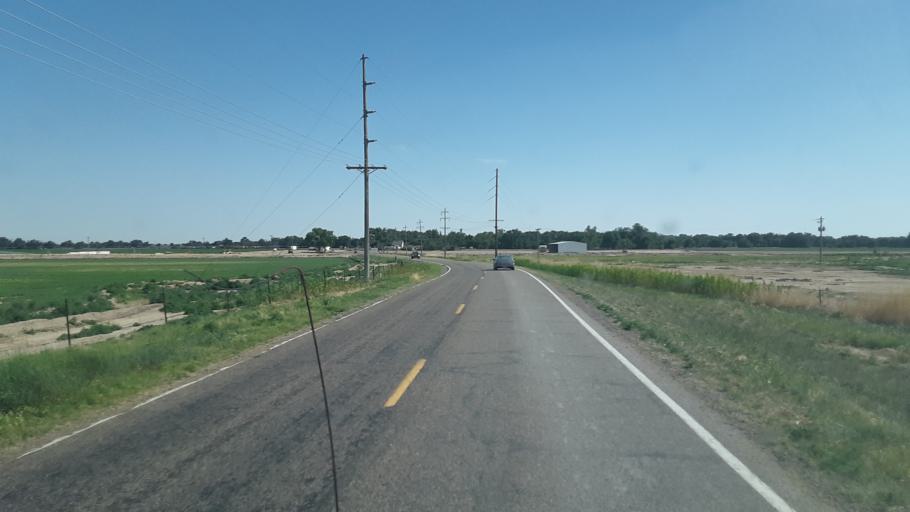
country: US
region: Colorado
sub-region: Crowley County
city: Ordway
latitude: 38.1187
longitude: -103.8641
